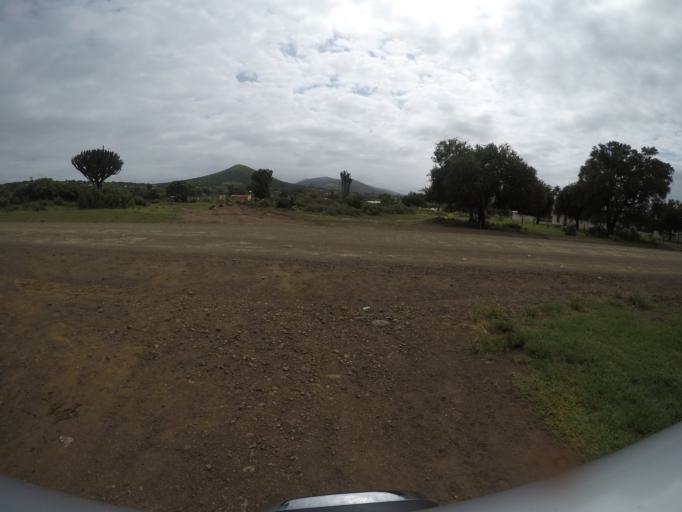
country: ZA
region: KwaZulu-Natal
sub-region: uThungulu District Municipality
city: Empangeni
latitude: -28.6155
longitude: 31.8487
